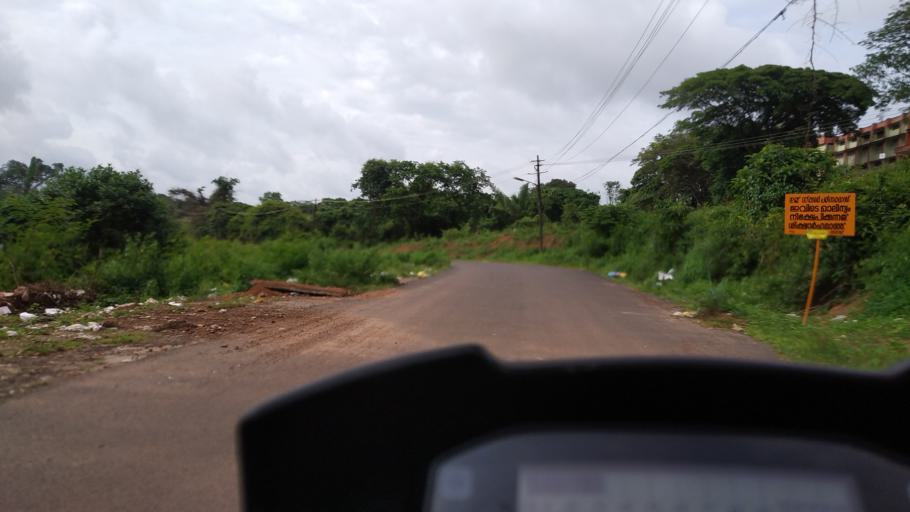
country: IN
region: Kerala
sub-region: Ernakulam
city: Aluva
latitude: 10.0521
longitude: 76.3443
